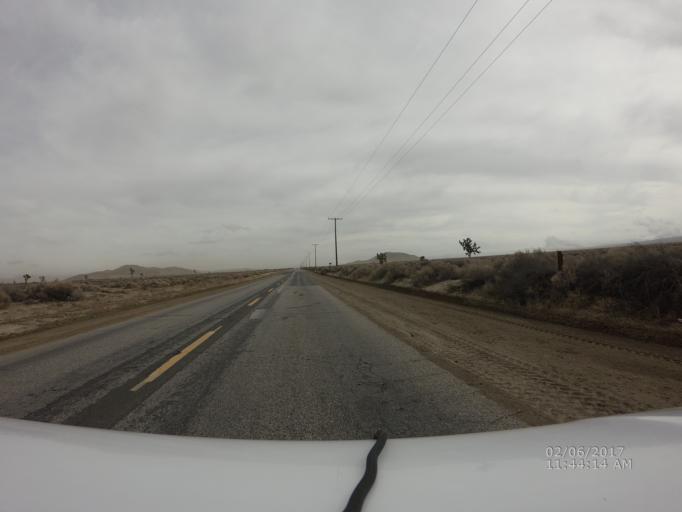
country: US
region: California
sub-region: Los Angeles County
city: Lake Los Angeles
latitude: 34.6019
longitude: -117.6829
